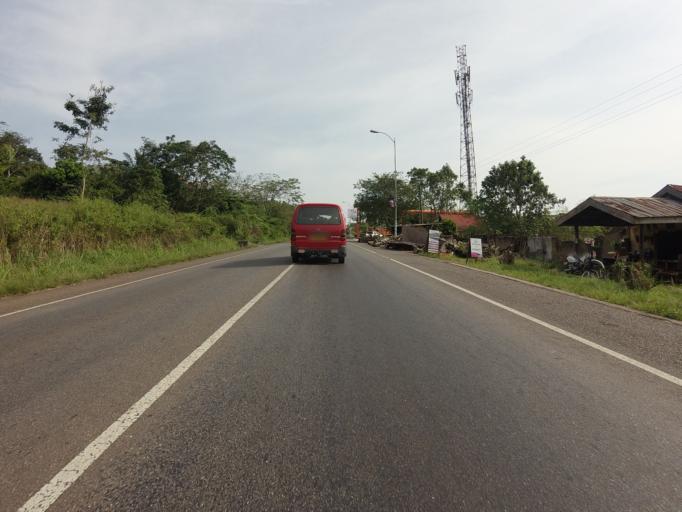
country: GH
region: Eastern
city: Aburi
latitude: 5.8325
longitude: -0.1833
